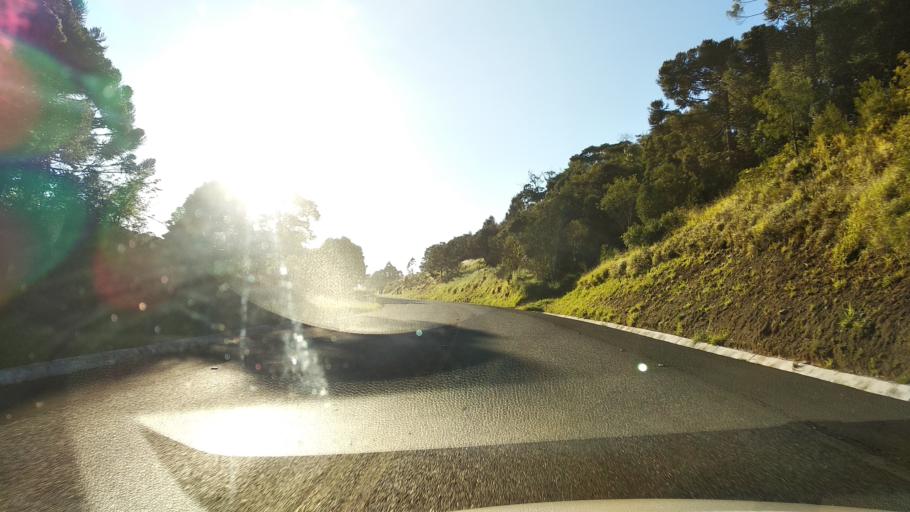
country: BR
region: Santa Catarina
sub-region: Correia Pinto
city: Correia Pinto
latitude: -27.6171
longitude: -50.6813
